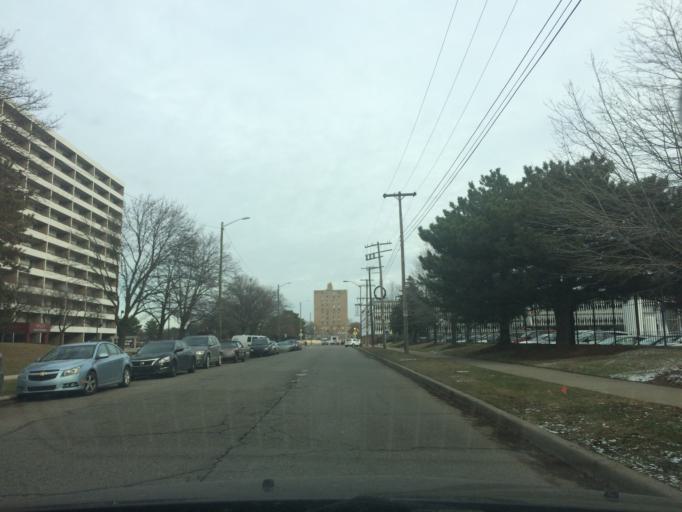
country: US
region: Michigan
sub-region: Wayne County
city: Highland Park
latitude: 42.3692
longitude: -83.0869
